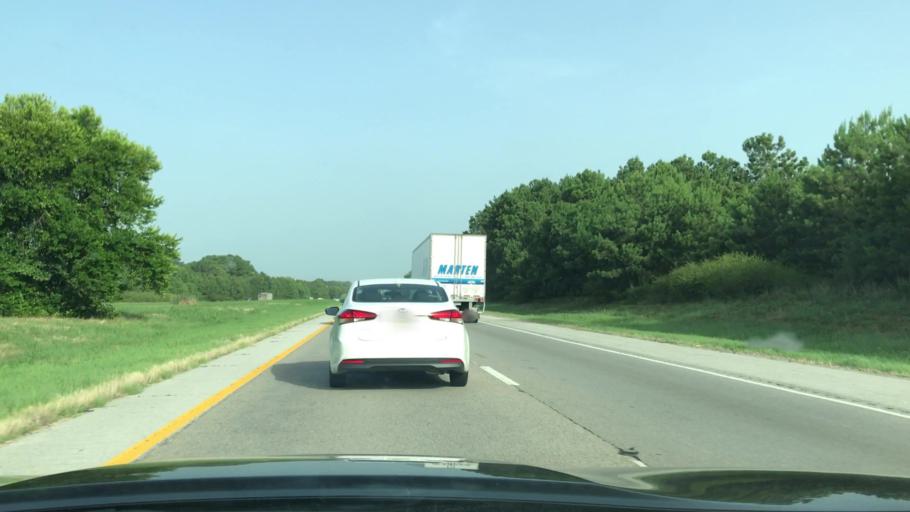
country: US
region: Texas
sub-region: Smith County
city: Hideaway
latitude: 32.4856
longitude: -95.5333
